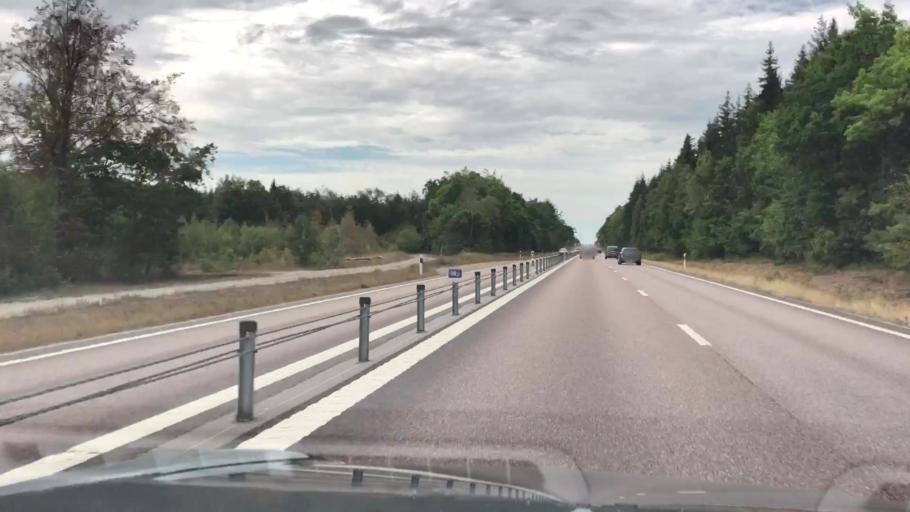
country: SE
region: Blekinge
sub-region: Karlskrona Kommun
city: Jaemjoe
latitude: 56.2212
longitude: 15.8994
